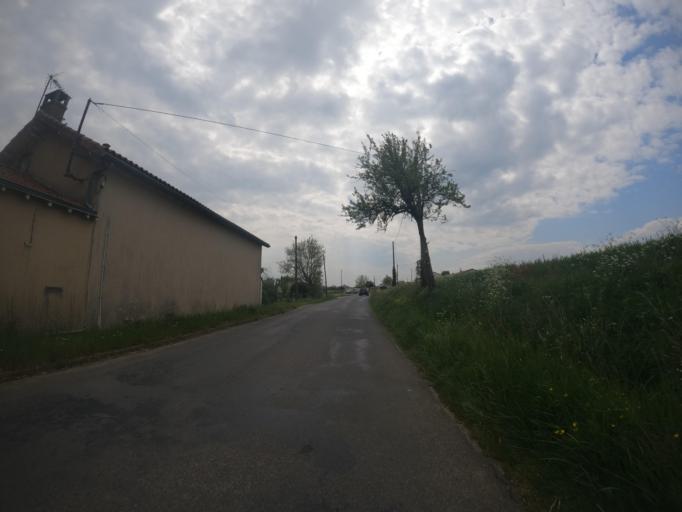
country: FR
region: Poitou-Charentes
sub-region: Departement des Deux-Sevres
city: Saint-Varent
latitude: 46.8710
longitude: -0.2946
